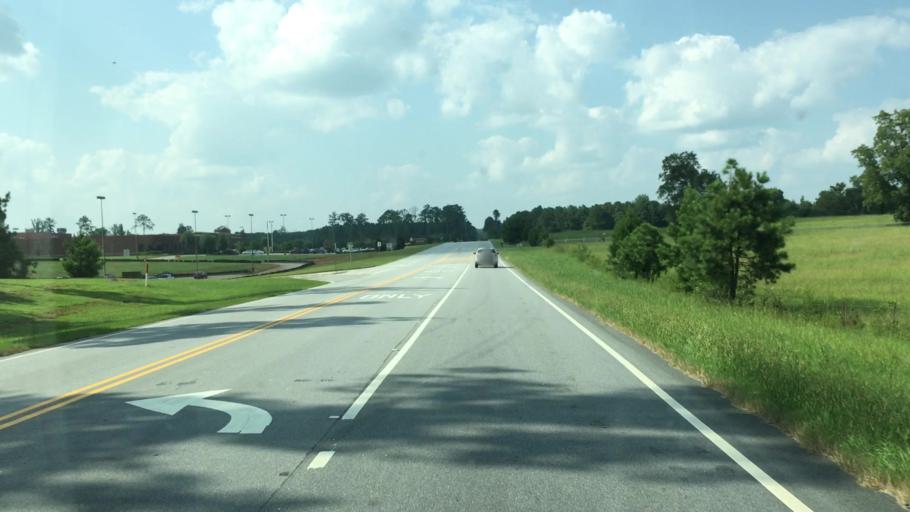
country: US
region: Georgia
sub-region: Jasper County
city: Monticello
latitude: 33.3341
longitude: -83.7115
